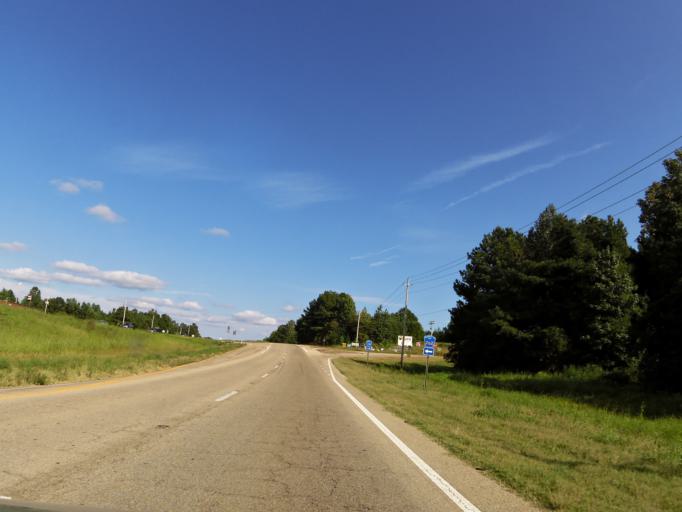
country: US
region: Mississippi
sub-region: Alcorn County
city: Farmington
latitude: 34.8631
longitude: -88.4137
